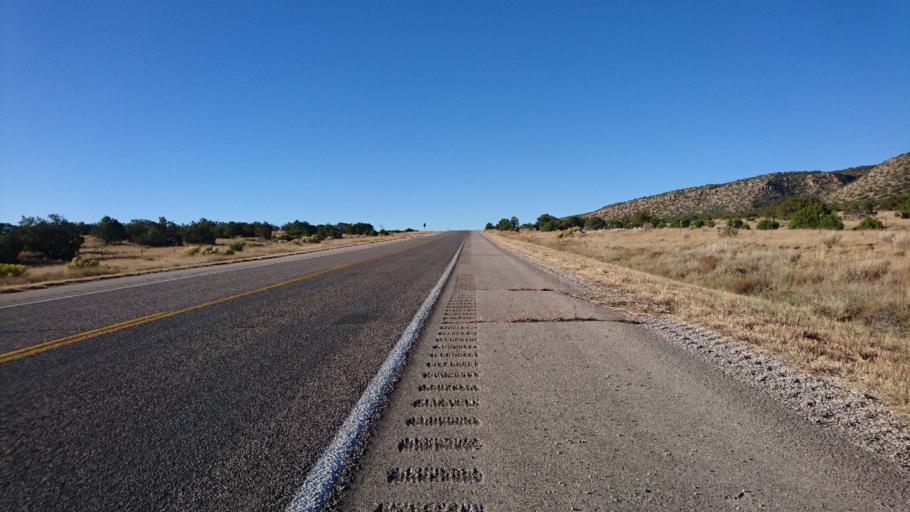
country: US
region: New Mexico
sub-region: Cibola County
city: Grants
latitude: 35.0031
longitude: -107.8938
